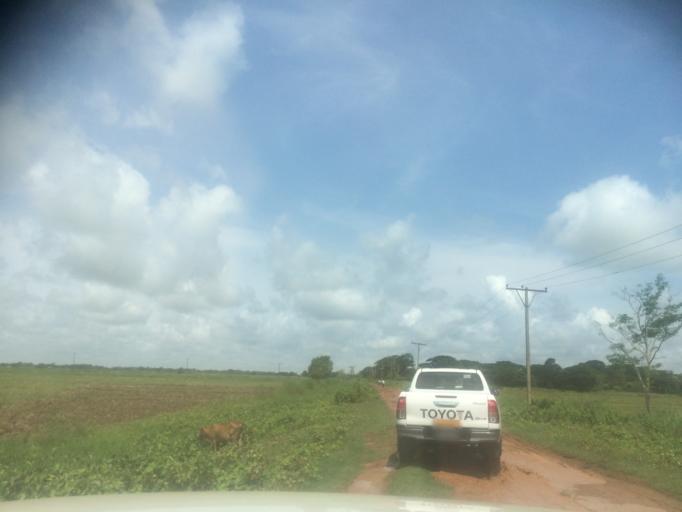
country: MM
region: Bago
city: Tharyarwady
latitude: 17.3175
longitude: 95.8997
